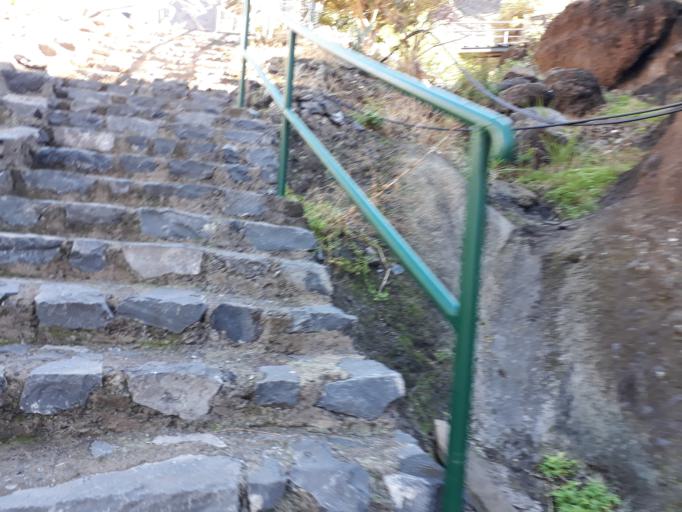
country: ES
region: Canary Islands
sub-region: Provincia de Santa Cruz de Tenerife
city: Vallehermosa
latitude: 28.1088
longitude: -17.3177
